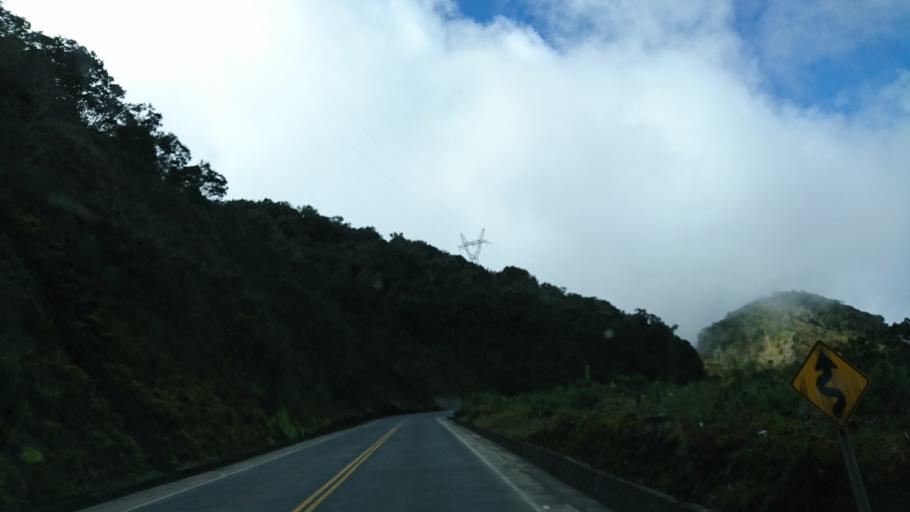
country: BO
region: La Paz
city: Coroico
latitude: -16.2853
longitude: -67.8428
